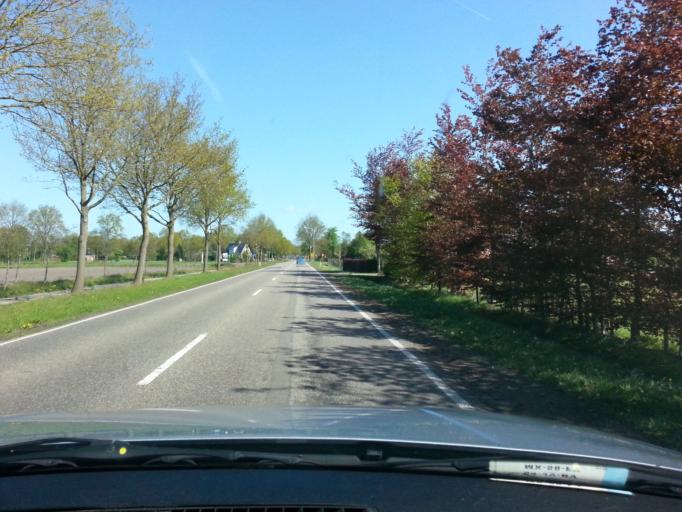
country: NL
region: Friesland
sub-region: Gemeente Achtkarspelen
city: Surhuisterveen
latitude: 53.1629
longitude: 6.1769
